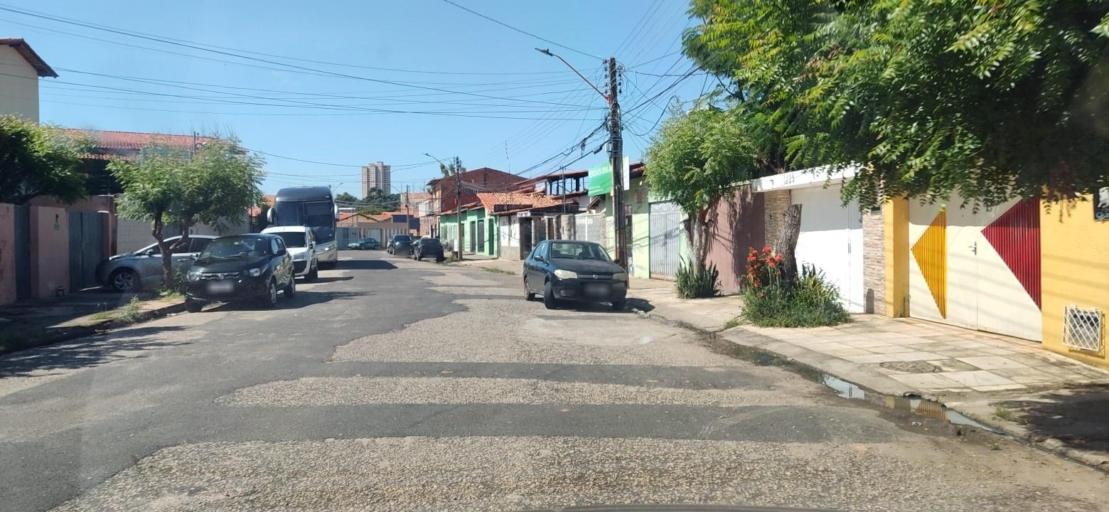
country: BR
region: Piaui
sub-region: Teresina
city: Teresina
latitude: -5.0998
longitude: -42.8018
